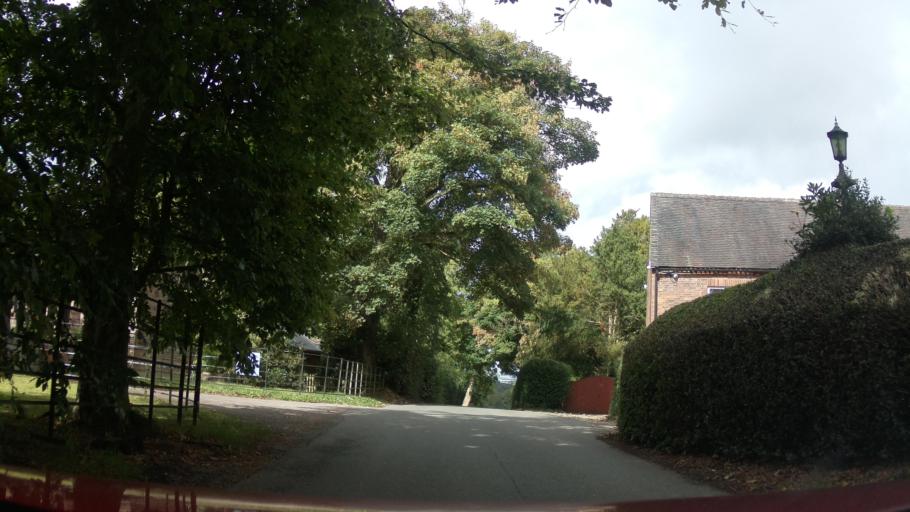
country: GB
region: England
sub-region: Staffordshire
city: Barlaston
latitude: 52.9496
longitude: -2.1577
